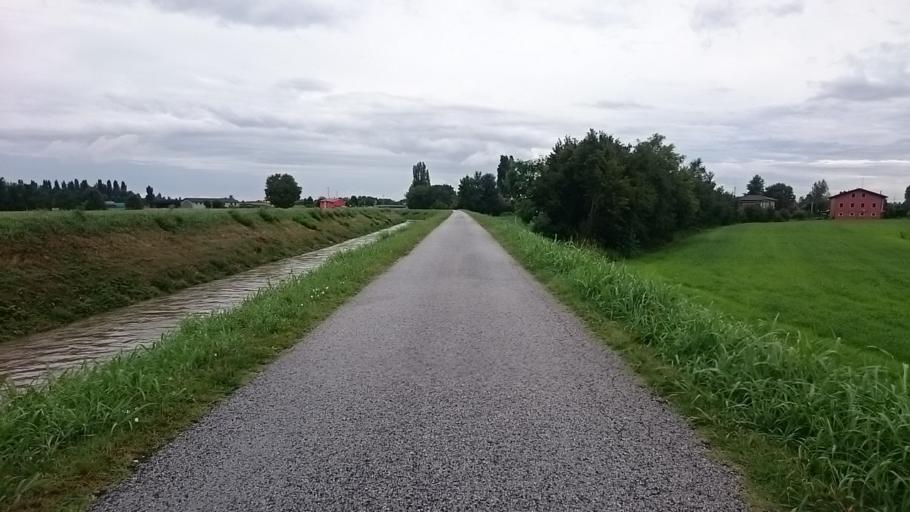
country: IT
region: Veneto
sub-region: Provincia di Padova
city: Loreggiola
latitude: 45.6043
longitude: 11.9319
